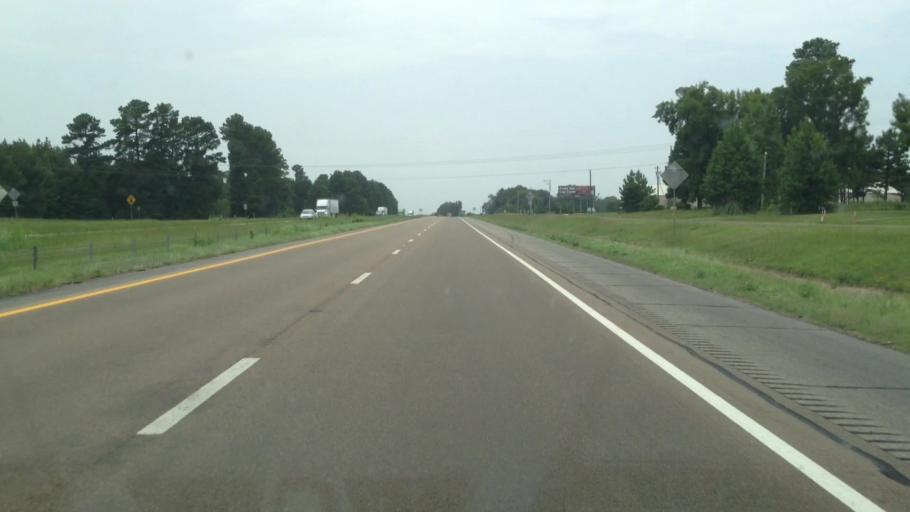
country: US
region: Texas
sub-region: Bowie County
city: New Boston
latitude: 33.4762
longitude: -94.4278
